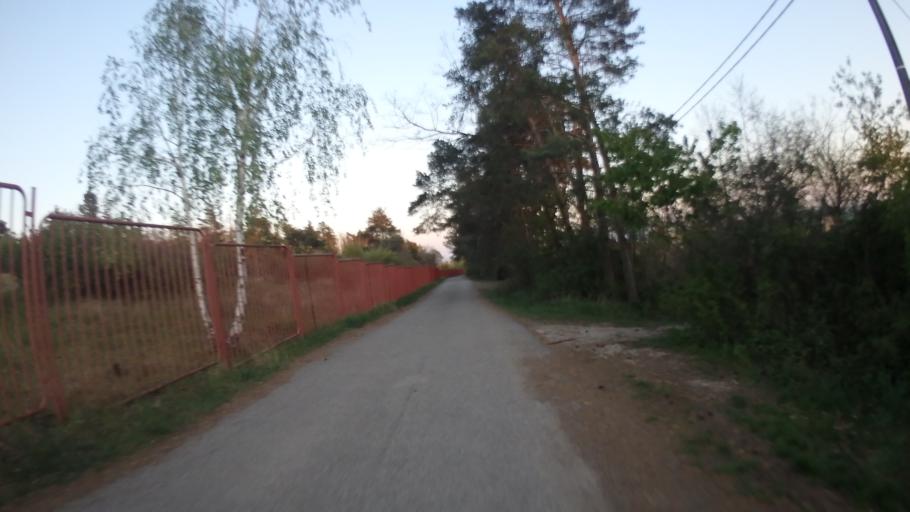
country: CZ
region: South Moravian
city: Ostopovice
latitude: 49.1830
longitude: 16.5514
